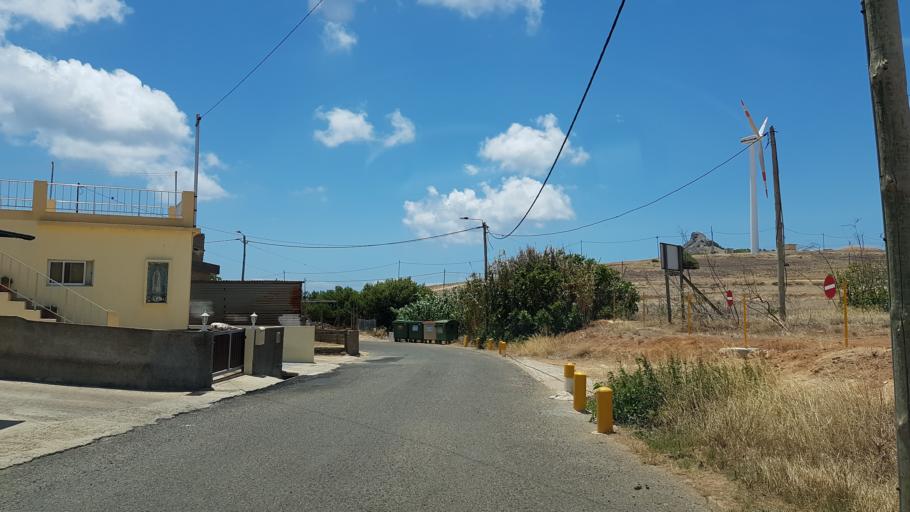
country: PT
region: Madeira
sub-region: Porto Santo
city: Vila de Porto Santo
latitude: 33.0617
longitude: -16.3605
